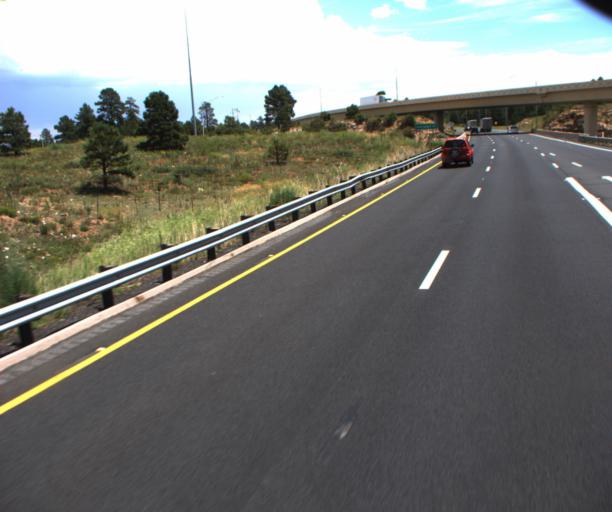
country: US
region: Arizona
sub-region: Coconino County
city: Flagstaff
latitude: 35.1719
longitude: -111.6634
